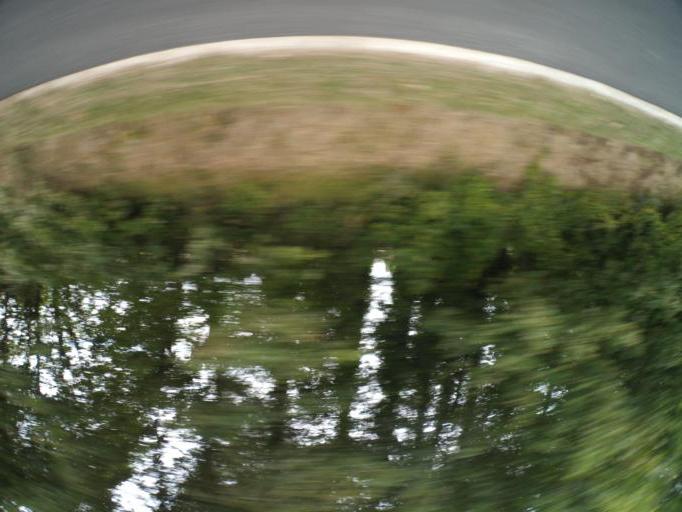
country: FR
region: Centre
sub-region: Departement d'Indre-et-Loire
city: Auzouer-en-Touraine
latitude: 47.5129
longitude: 0.9284
